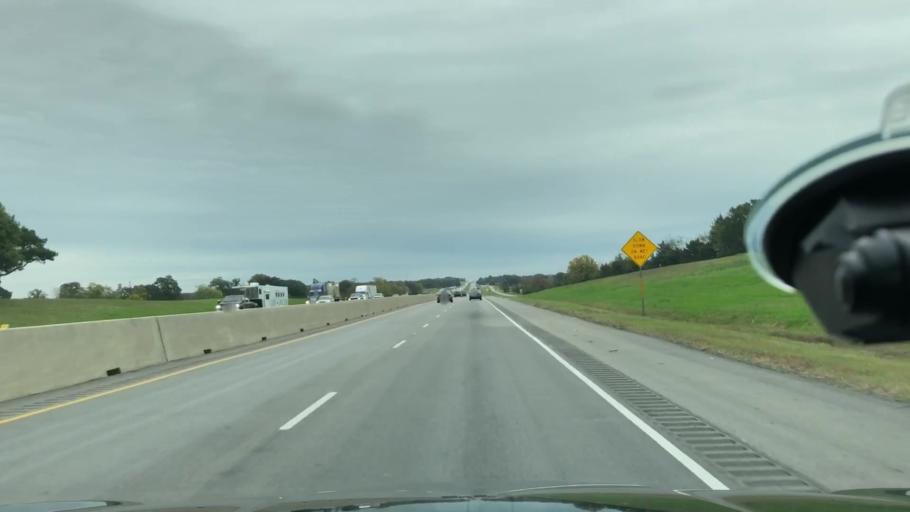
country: US
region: Texas
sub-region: Franklin County
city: Mount Vernon
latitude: 33.1660
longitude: -95.3067
